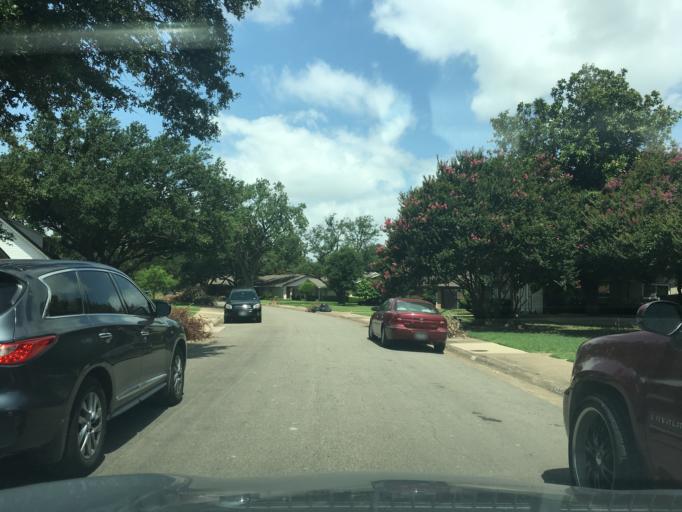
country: US
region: Texas
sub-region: Dallas County
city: Addison
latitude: 32.9228
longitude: -96.8236
